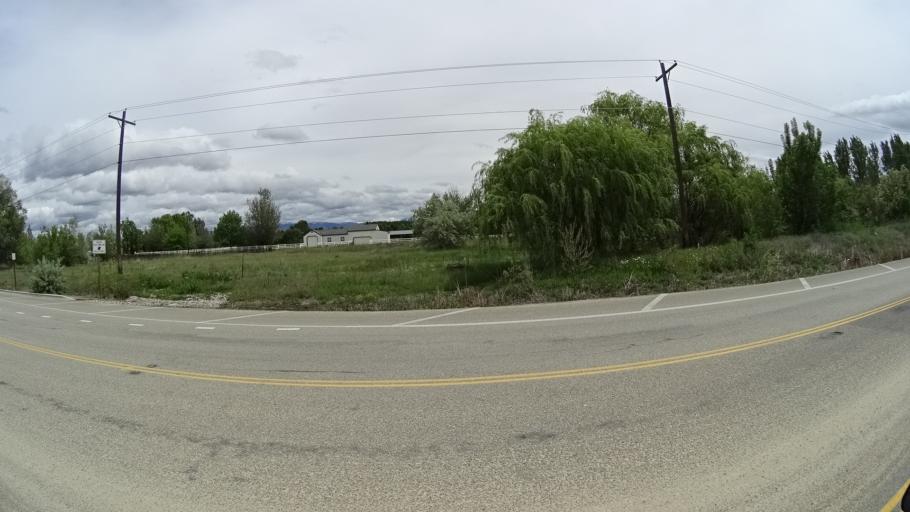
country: US
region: Idaho
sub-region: Ada County
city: Eagle
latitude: 43.6927
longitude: -116.4137
